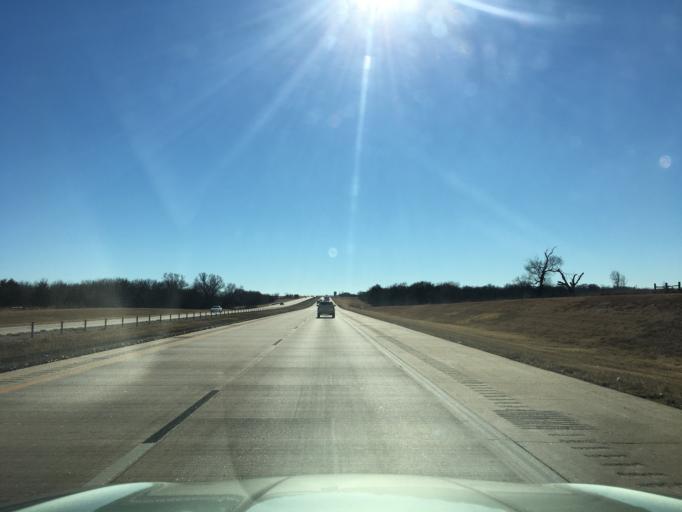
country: US
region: Oklahoma
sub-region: Noble County
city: Perry
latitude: 36.4410
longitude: -97.3271
